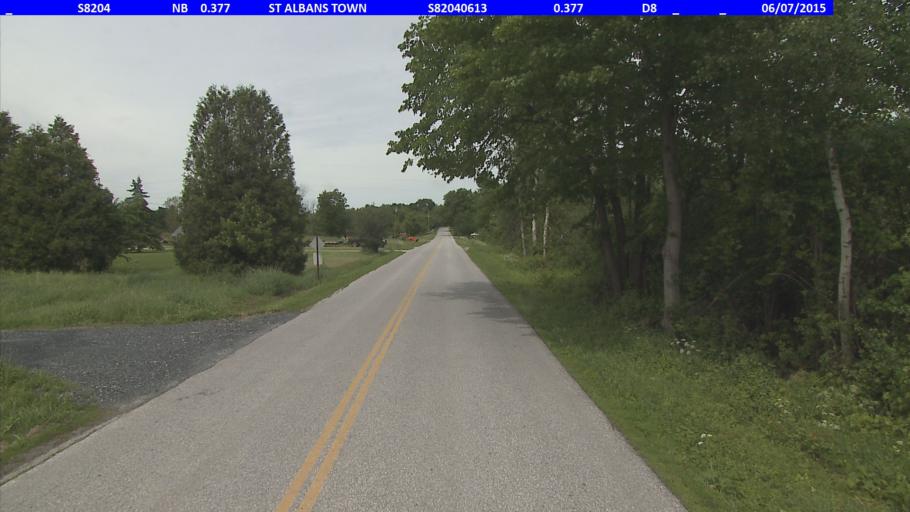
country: US
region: Vermont
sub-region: Franklin County
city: Saint Albans
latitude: 44.8081
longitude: -73.1107
